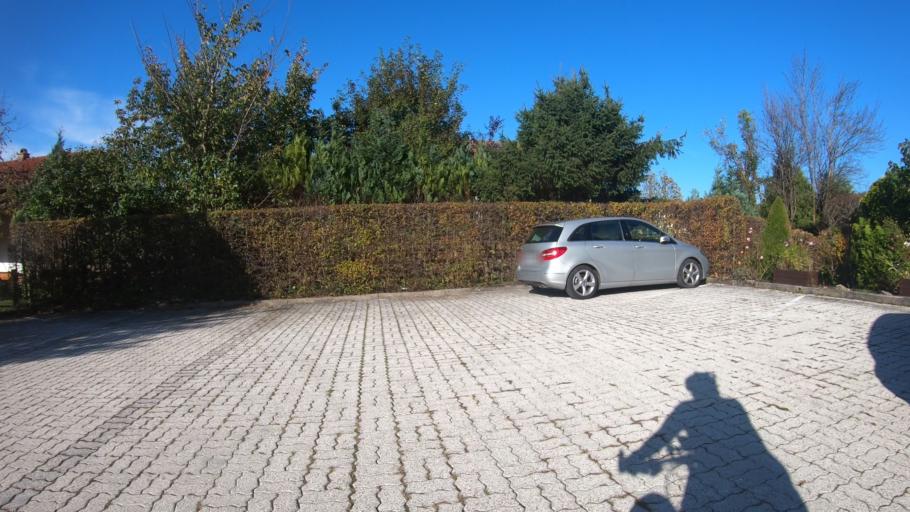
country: DE
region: Bavaria
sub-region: Upper Bavaria
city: Bergen
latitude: 47.8029
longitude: 12.5896
